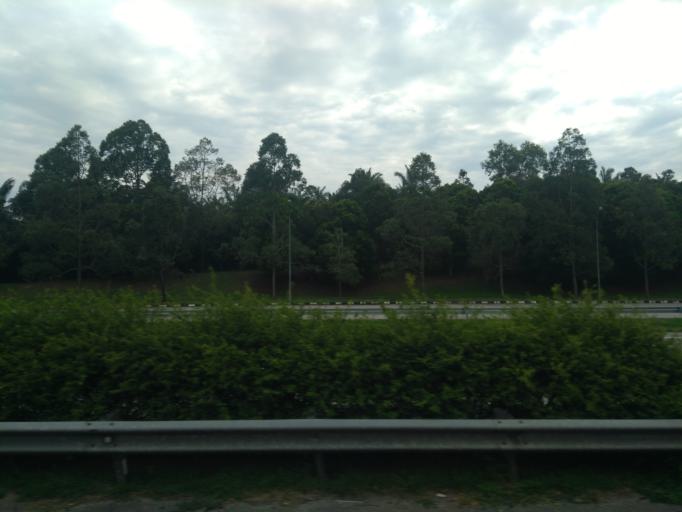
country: MY
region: Melaka
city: Alor Gajah
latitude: 2.3945
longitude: 102.2229
